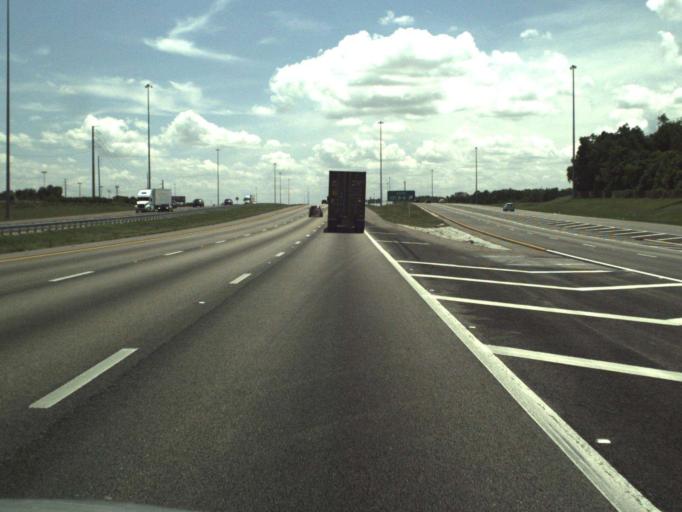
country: US
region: Florida
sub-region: Seminole County
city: Lake Mary
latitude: 28.8072
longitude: -81.3403
